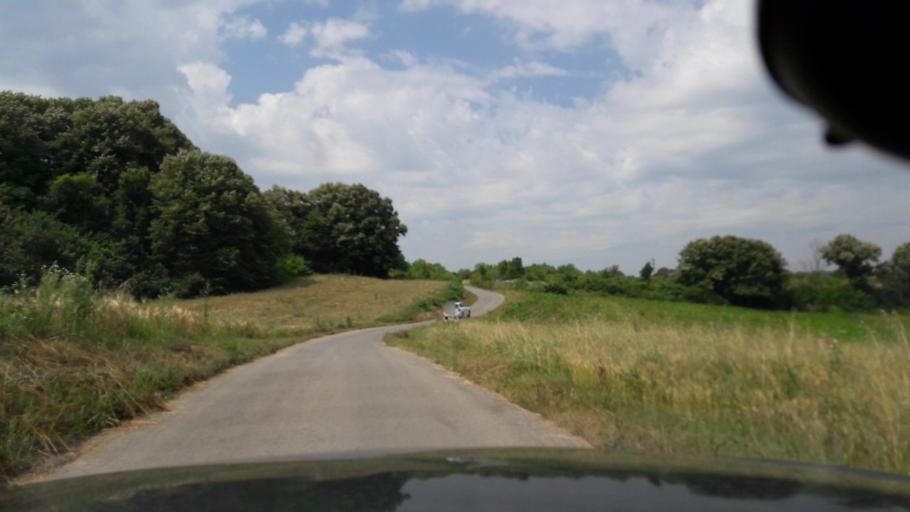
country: RS
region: Central Serbia
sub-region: Belgrade
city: Sopot
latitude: 44.6174
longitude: 20.6021
